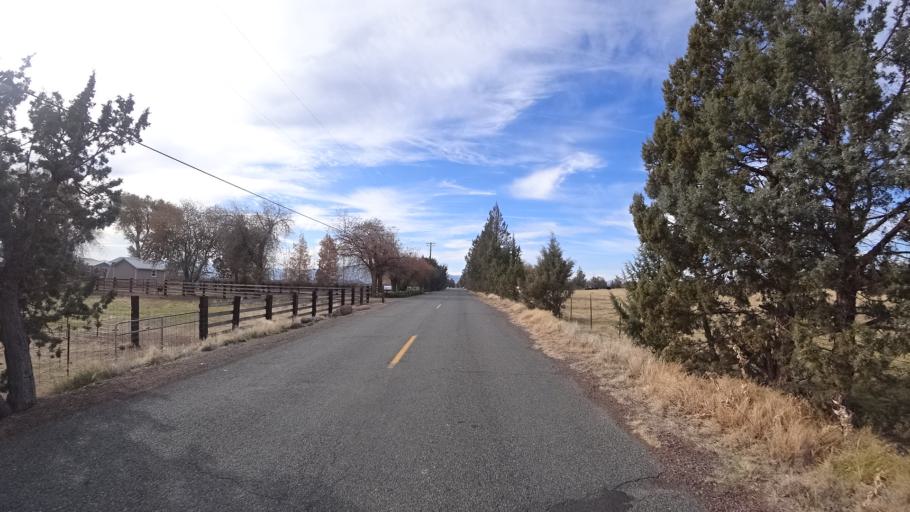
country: US
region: California
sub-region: Siskiyou County
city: Montague
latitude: 41.6384
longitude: -122.4157
